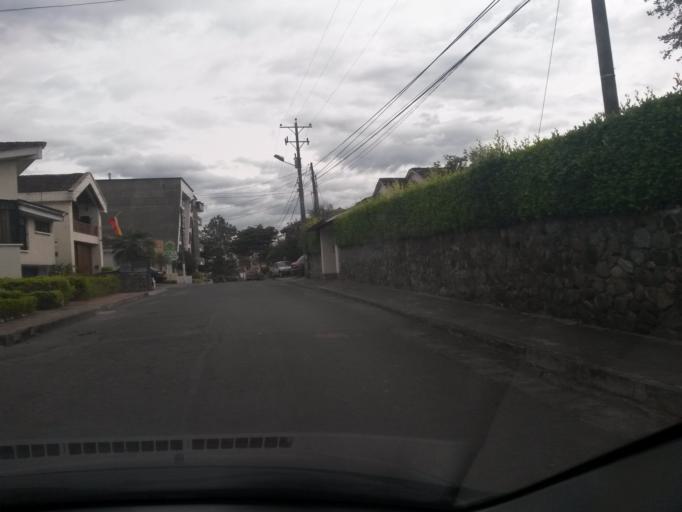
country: CO
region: Cauca
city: Popayan
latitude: 2.4580
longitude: -76.5957
